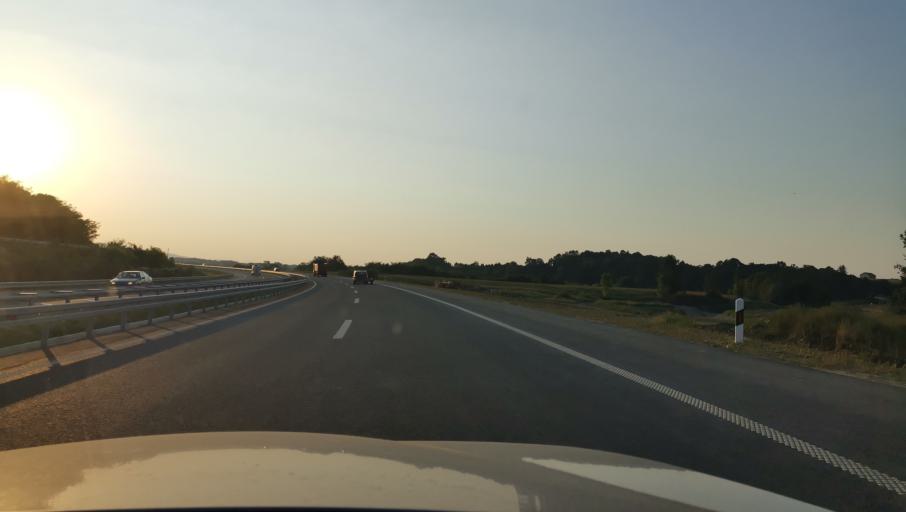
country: RS
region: Central Serbia
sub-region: Kolubarski Okrug
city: Lajkovac
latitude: 44.3422
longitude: 20.1941
